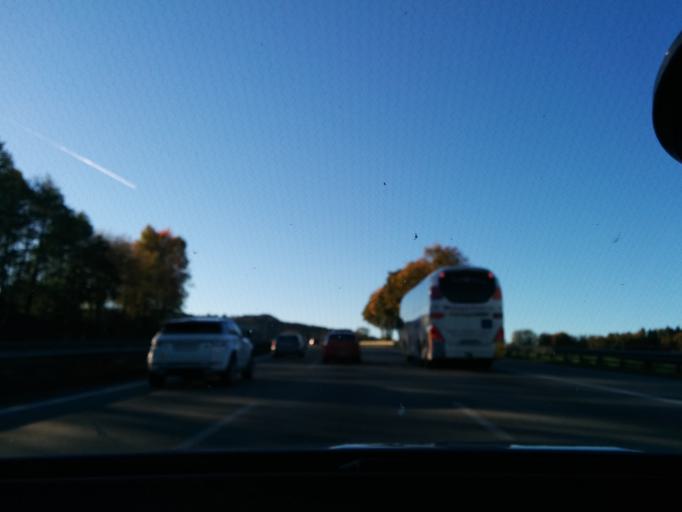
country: DE
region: Bavaria
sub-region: Upper Bavaria
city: Irschenberg
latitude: 47.8259
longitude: 11.9595
